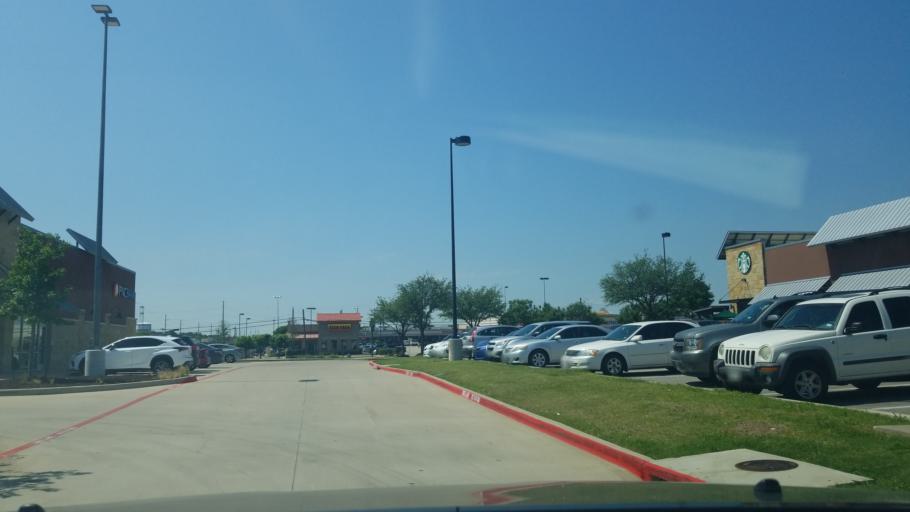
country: US
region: Texas
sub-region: Denton County
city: Denton
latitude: 33.2306
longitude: -97.1617
